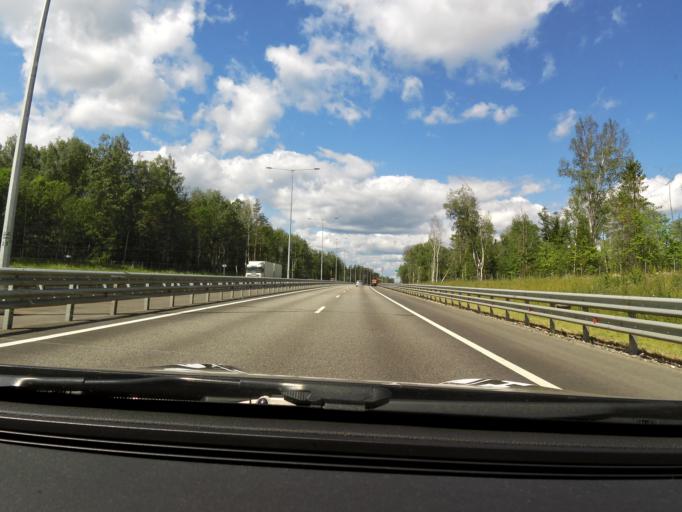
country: RU
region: Tverskaya
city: Vyshniy Volochek
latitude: 57.3760
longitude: 34.5885
